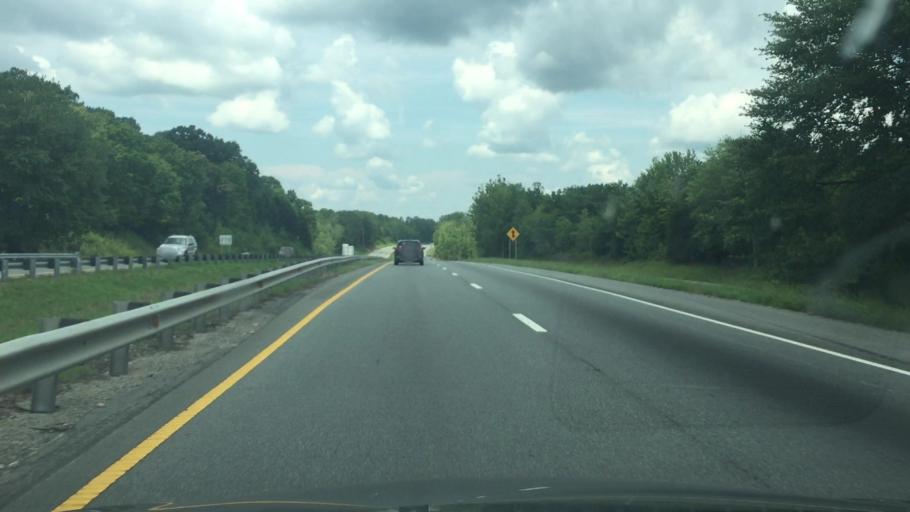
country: US
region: North Carolina
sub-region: Randolph County
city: Asheboro
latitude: 35.6207
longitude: -79.8260
